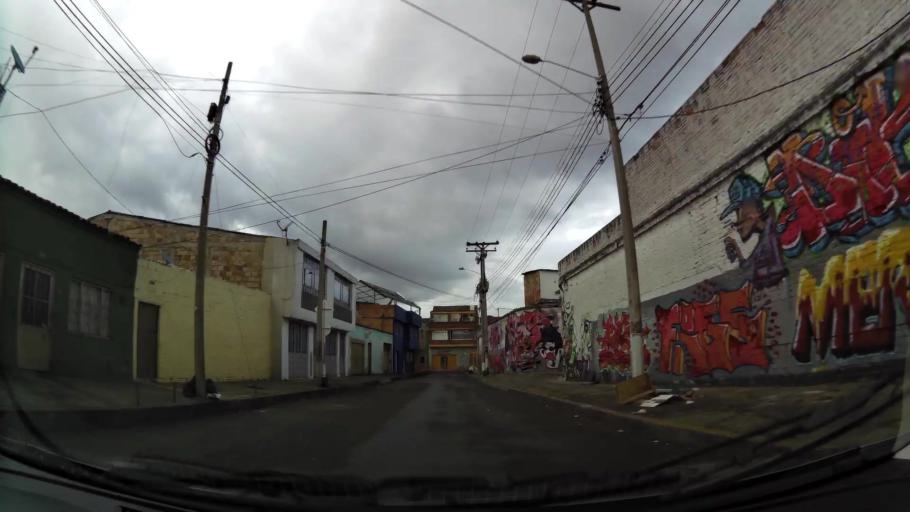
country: CO
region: Bogota D.C.
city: Barrio San Luis
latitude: 4.6736
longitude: -74.0768
